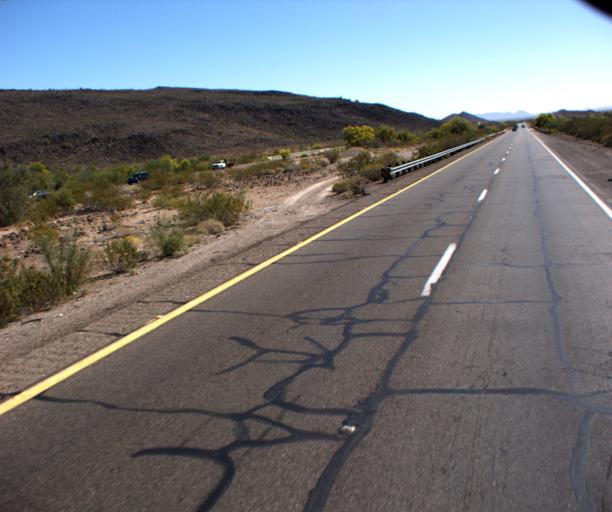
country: US
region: Arizona
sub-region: La Paz County
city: Quartzsite
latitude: 33.6495
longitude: -113.9111
